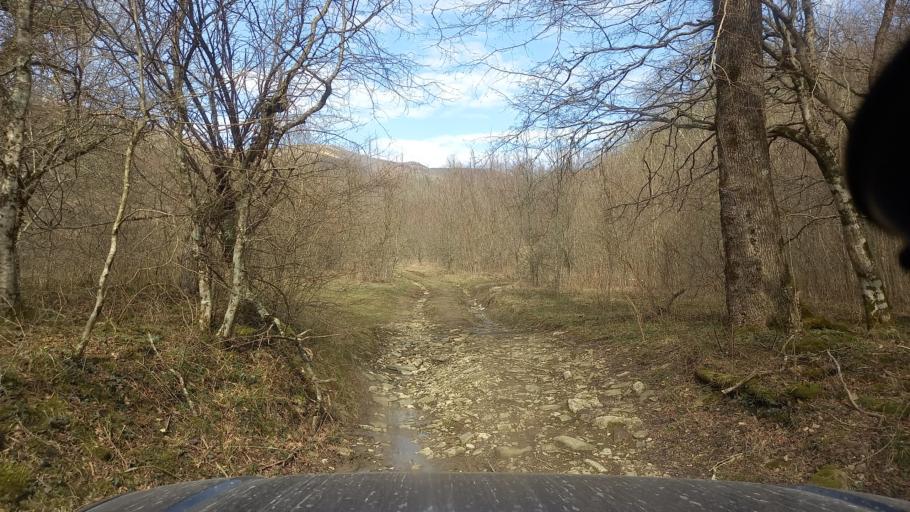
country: RU
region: Krasnodarskiy
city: Arkhipo-Osipovka
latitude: 44.3788
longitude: 38.5981
